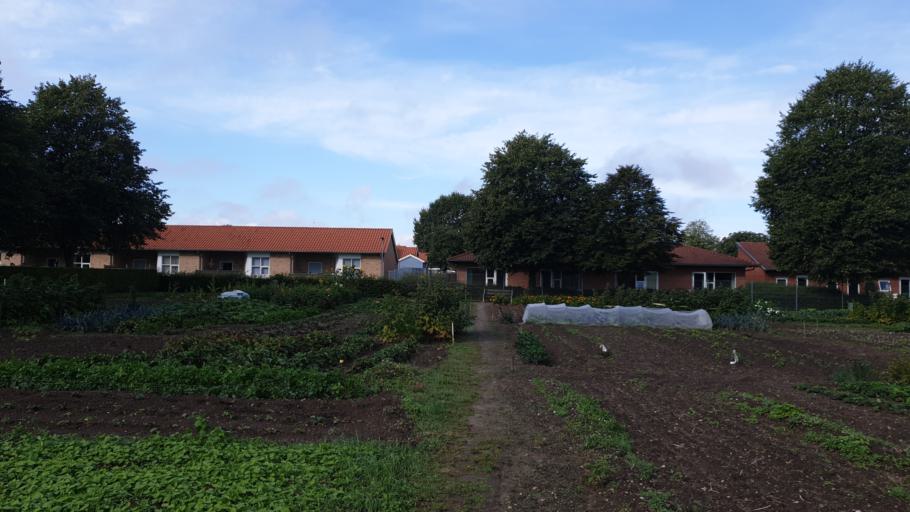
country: DK
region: Central Jutland
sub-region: Hedensted Kommune
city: Hedensted
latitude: 55.8057
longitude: 9.6958
